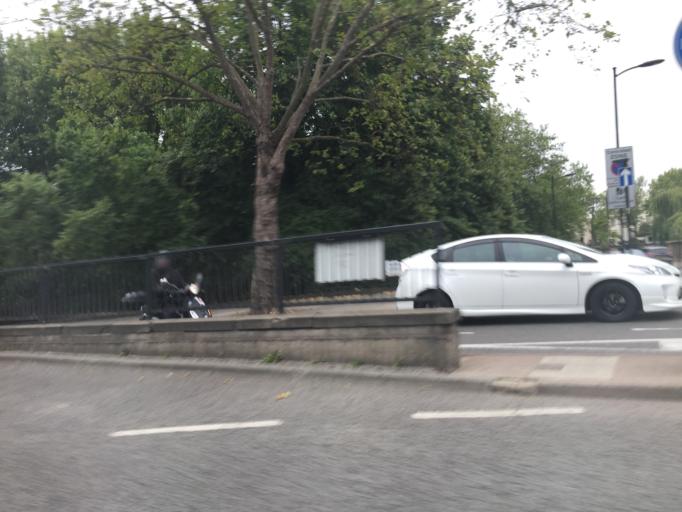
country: GB
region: England
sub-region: Greater London
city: Bayswater
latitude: 51.5204
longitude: -0.1814
